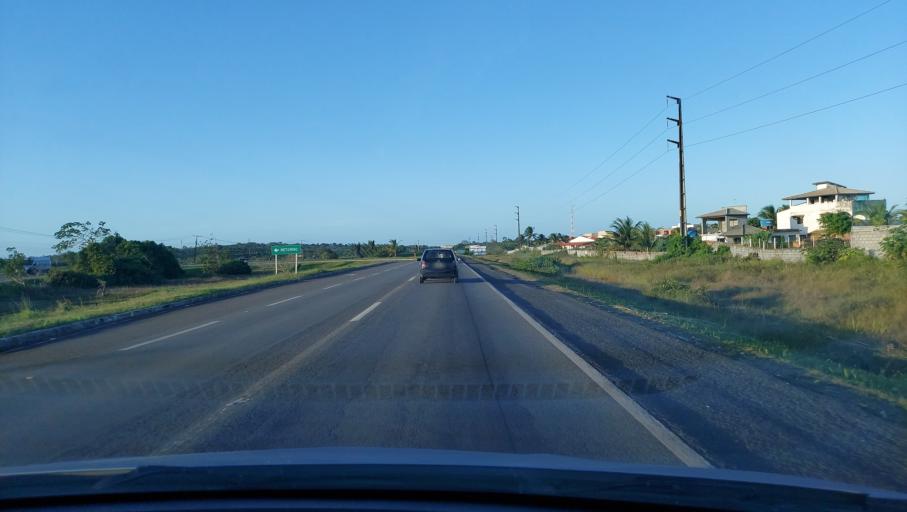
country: BR
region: Bahia
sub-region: Camacari
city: Camacari
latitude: -12.7316
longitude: -38.1628
